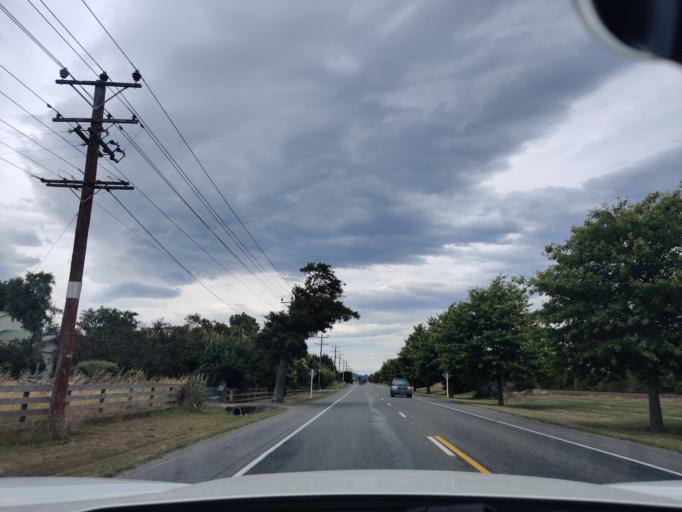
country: NZ
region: Wellington
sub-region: Masterton District
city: Masterton
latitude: -40.9560
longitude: 175.6191
